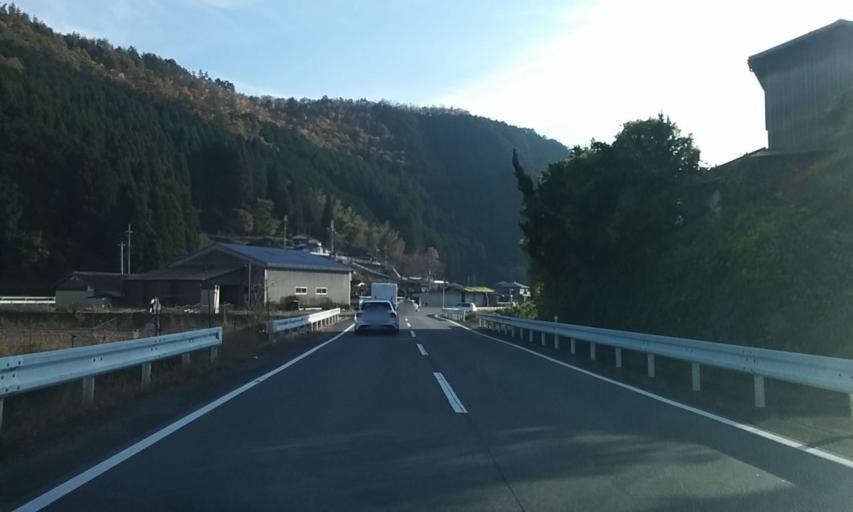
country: JP
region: Kyoto
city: Kameoka
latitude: 35.1921
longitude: 135.5210
